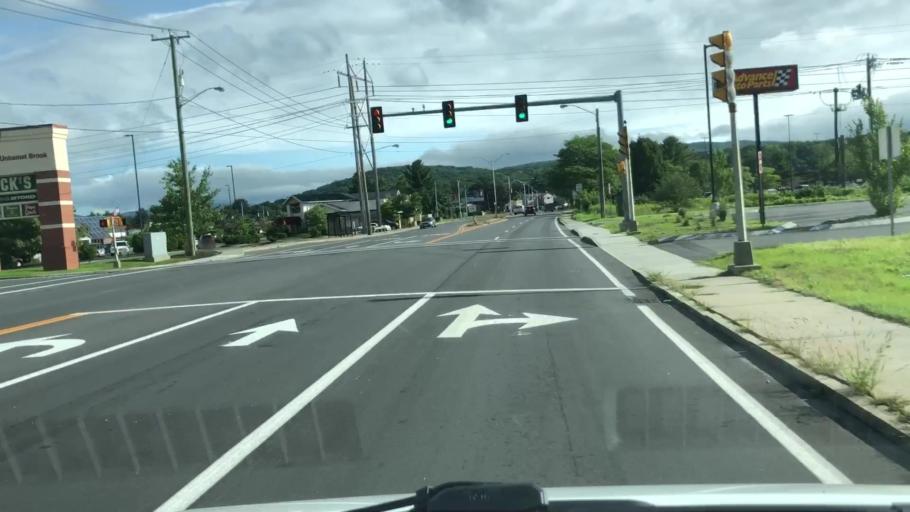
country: US
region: Massachusetts
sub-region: Berkshire County
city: Dalton
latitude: 42.4647
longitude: -73.2056
